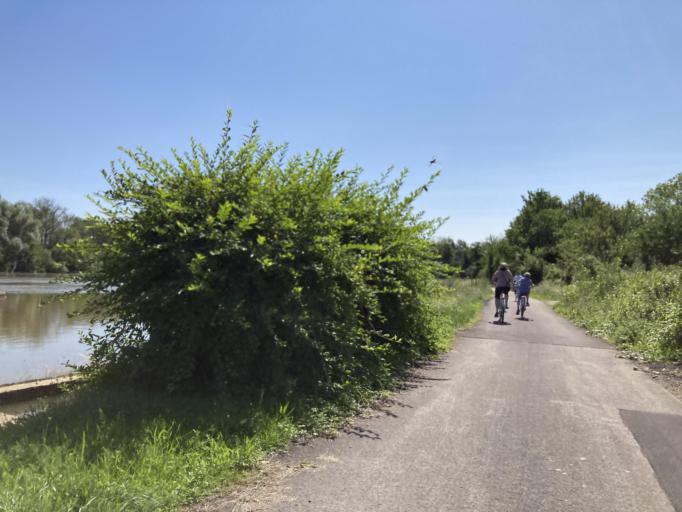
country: FR
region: Bourgogne
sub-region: Departement de l'Yonne
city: Joigny
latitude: 47.9699
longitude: 3.4244
